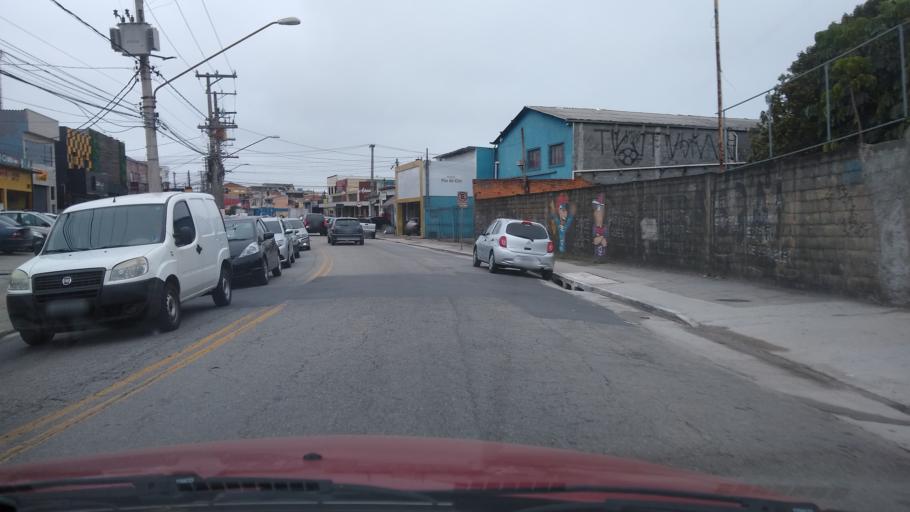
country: BR
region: Sao Paulo
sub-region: Diadema
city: Diadema
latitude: -23.6273
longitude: -46.6192
